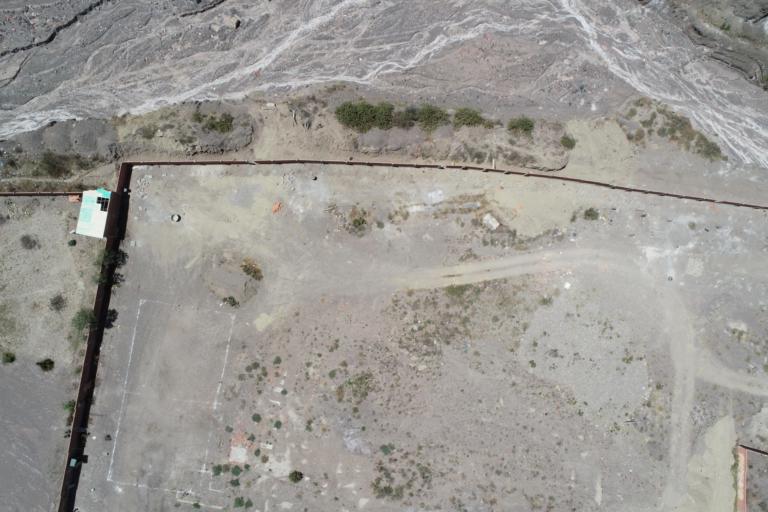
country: BO
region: La Paz
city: La Paz
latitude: -16.6442
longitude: -68.0400
